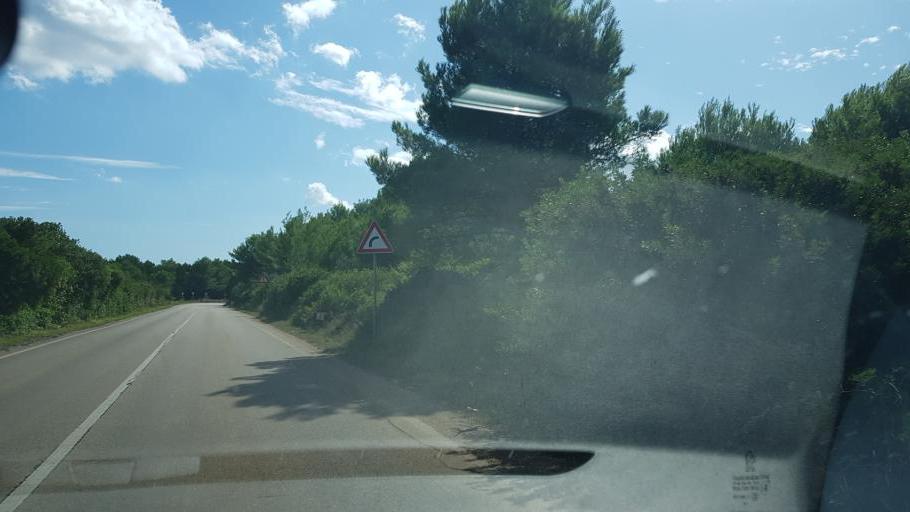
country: IT
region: Apulia
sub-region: Provincia di Lecce
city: Borgagne
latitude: 40.2410
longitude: 18.4437
